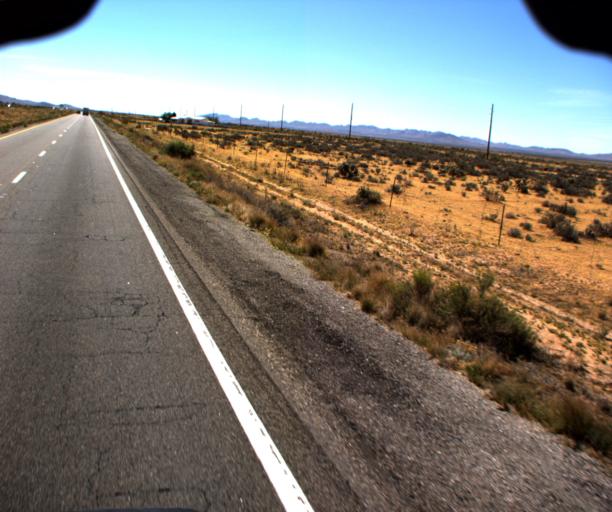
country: US
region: Arizona
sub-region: Mohave County
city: Dolan Springs
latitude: 35.5500
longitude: -114.3668
